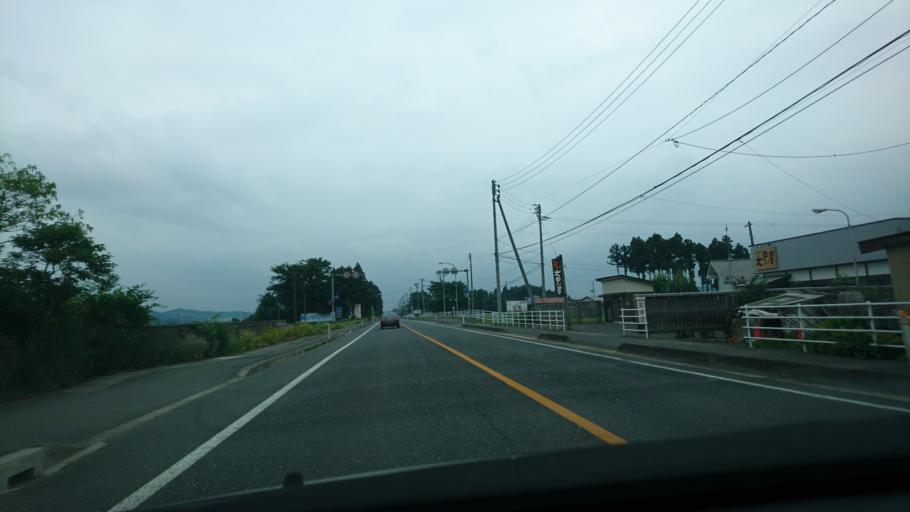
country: JP
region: Miyagi
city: Furukawa
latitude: 38.6892
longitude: 140.8504
